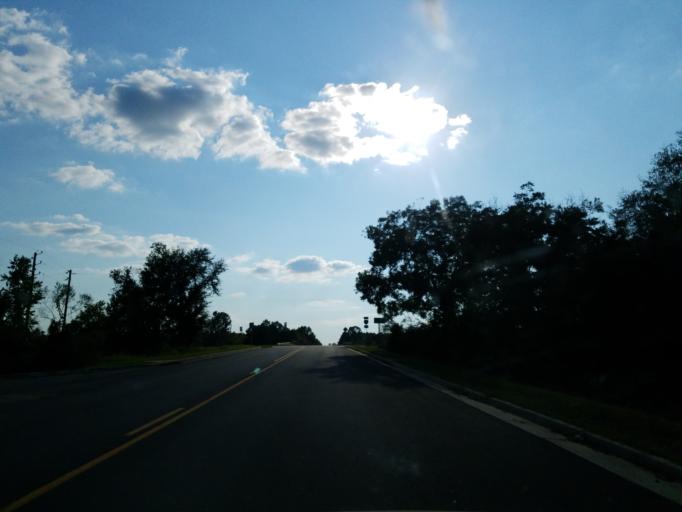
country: US
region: Georgia
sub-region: Cook County
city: Sparks
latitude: 31.1663
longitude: -83.4480
